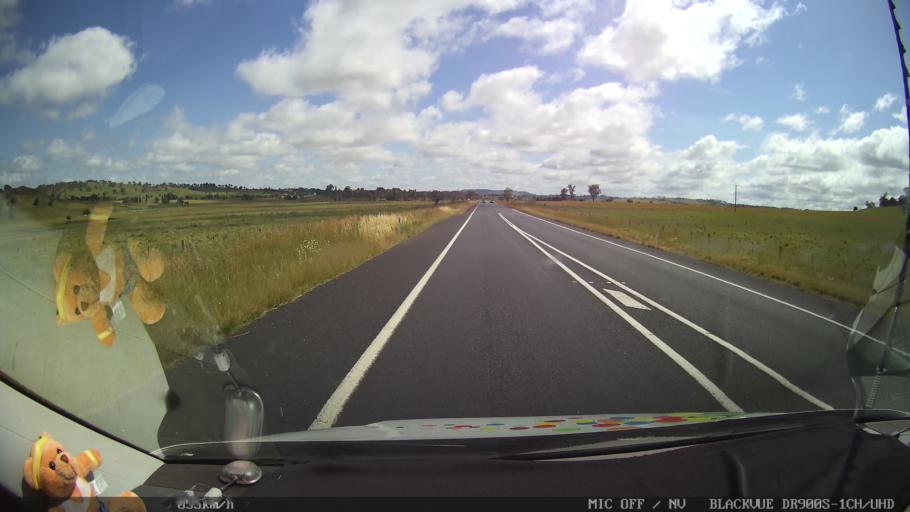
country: AU
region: New South Wales
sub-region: Glen Innes Severn
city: Glen Innes
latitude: -29.9450
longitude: 151.7203
